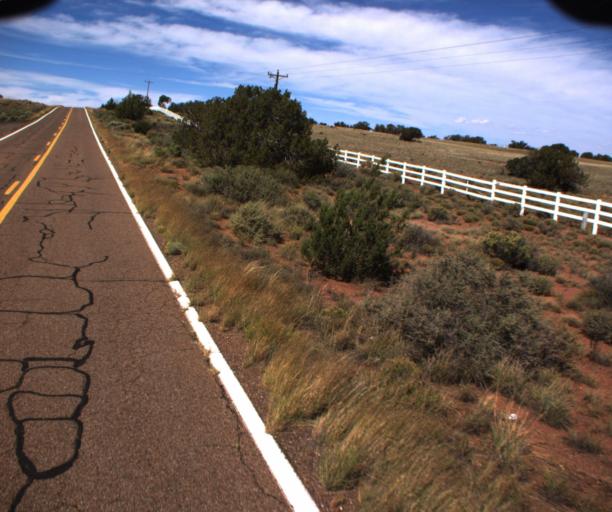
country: US
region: Arizona
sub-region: Apache County
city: Saint Johns
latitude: 34.5795
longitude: -109.6399
